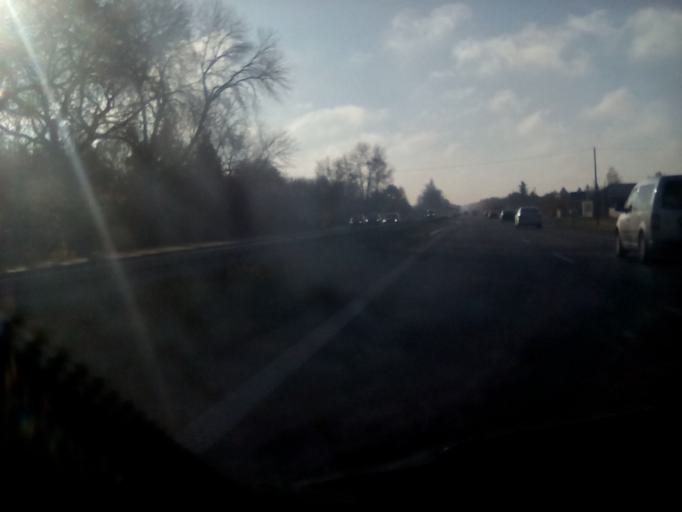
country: PL
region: Masovian Voivodeship
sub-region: Powiat piaseczynski
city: Tarczyn
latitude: 51.9335
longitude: 20.8482
